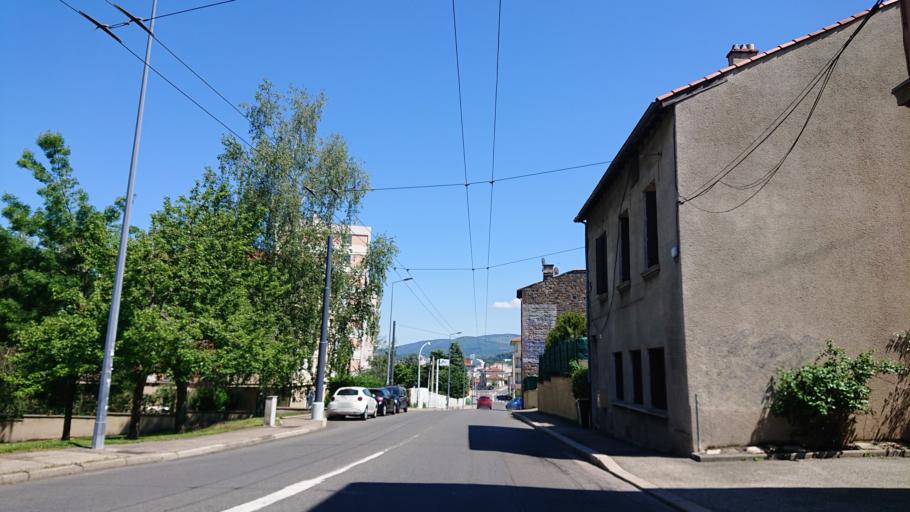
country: FR
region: Rhone-Alpes
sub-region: Departement de la Loire
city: Saint-Etienne
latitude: 45.4432
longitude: 4.3702
